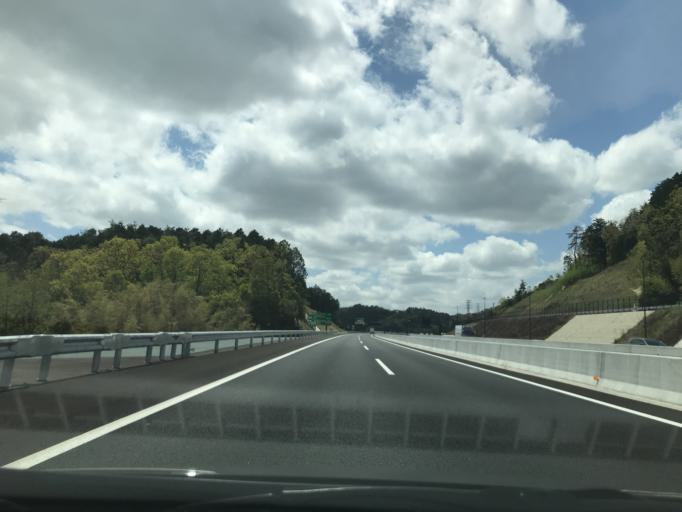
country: JP
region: Osaka
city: Ibaraki
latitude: 34.8779
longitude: 135.5271
